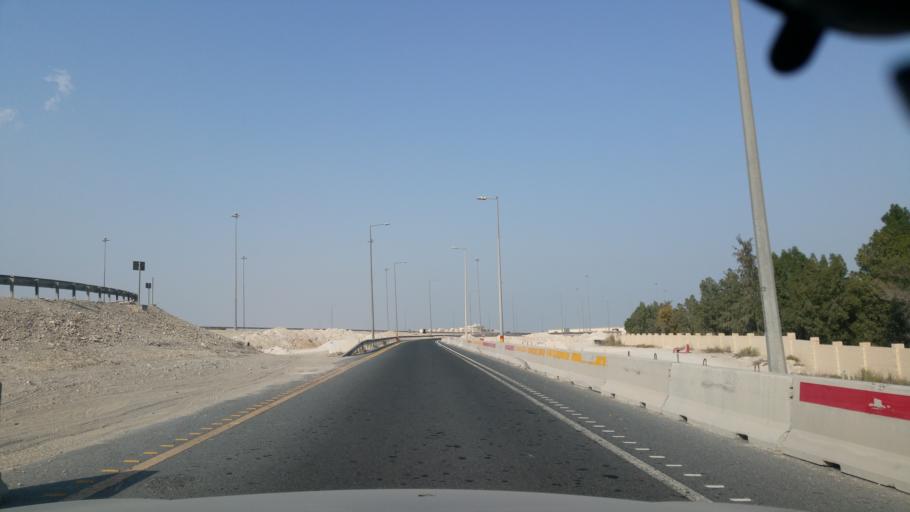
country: QA
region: Baladiyat Umm Salal
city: Umm Salal `Ali
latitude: 25.4468
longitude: 51.4117
